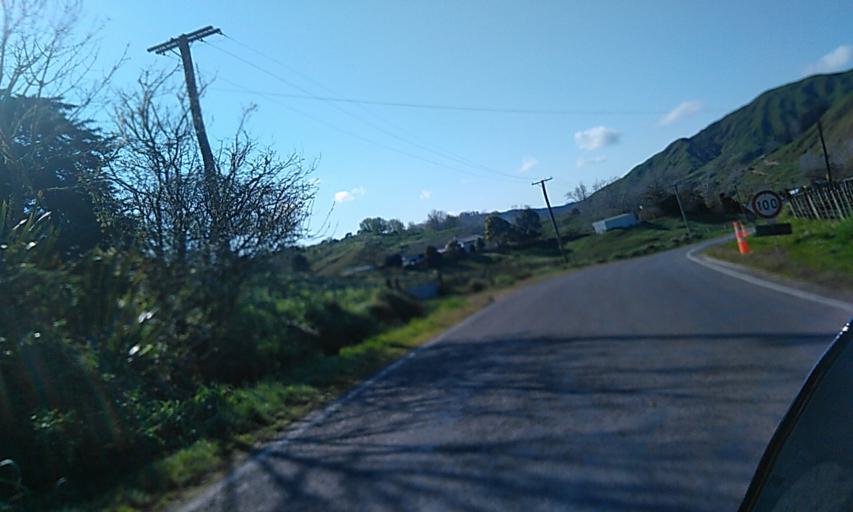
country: NZ
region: Gisborne
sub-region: Gisborne District
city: Gisborne
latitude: -38.5027
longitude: 178.0534
